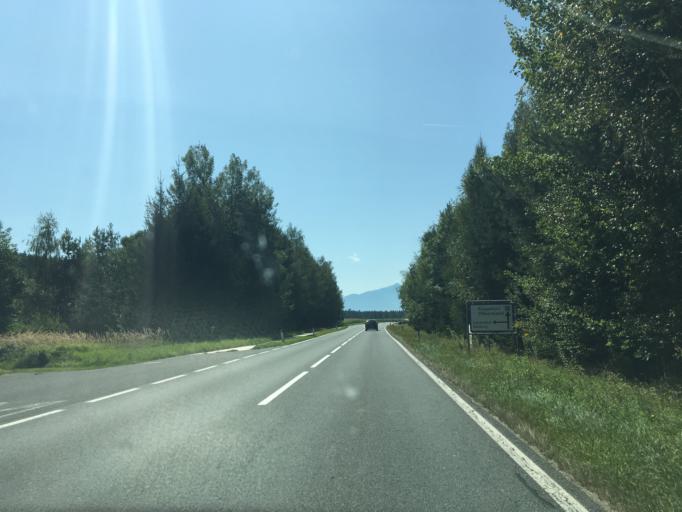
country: AT
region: Carinthia
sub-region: Politischer Bezirk Volkermarkt
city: Voelkermarkt
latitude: 46.6722
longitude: 14.6664
